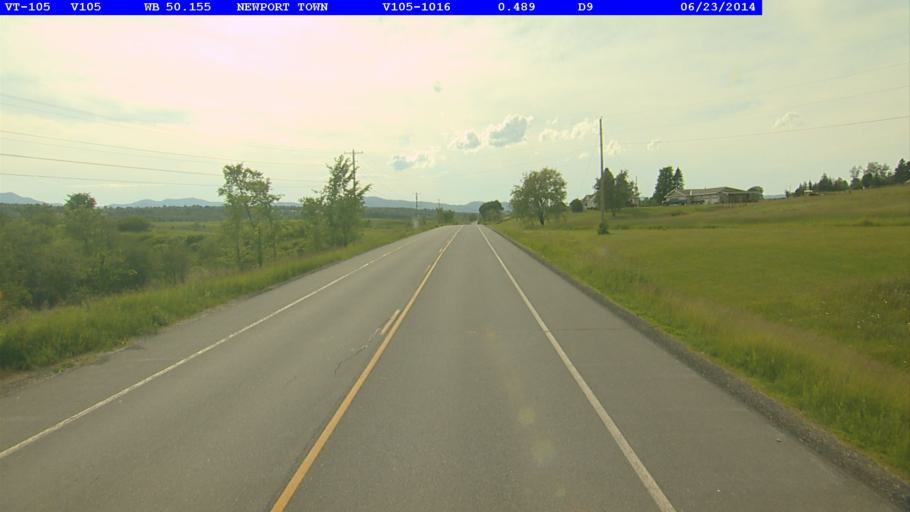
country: US
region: Vermont
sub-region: Orleans County
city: Newport
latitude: 44.9754
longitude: -72.3268
